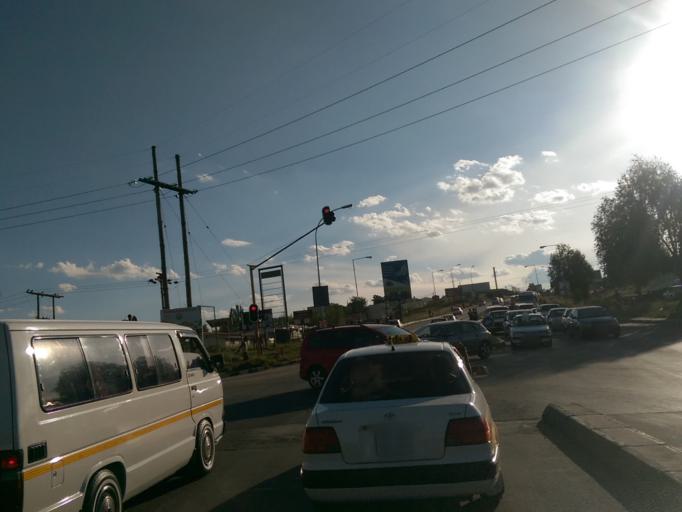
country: LS
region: Maseru
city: Maseru
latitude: -29.3127
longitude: 27.5100
